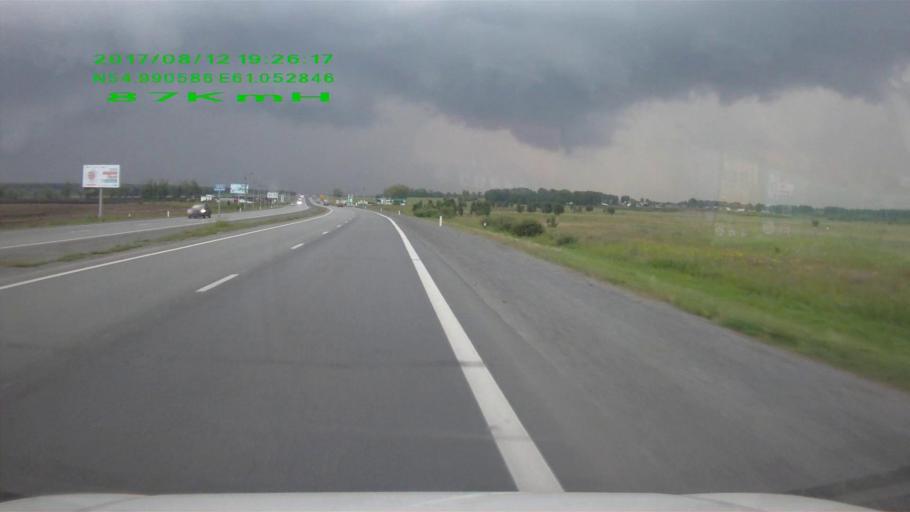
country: RU
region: Chelyabinsk
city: Poletayevo
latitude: 54.9900
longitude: 61.0493
